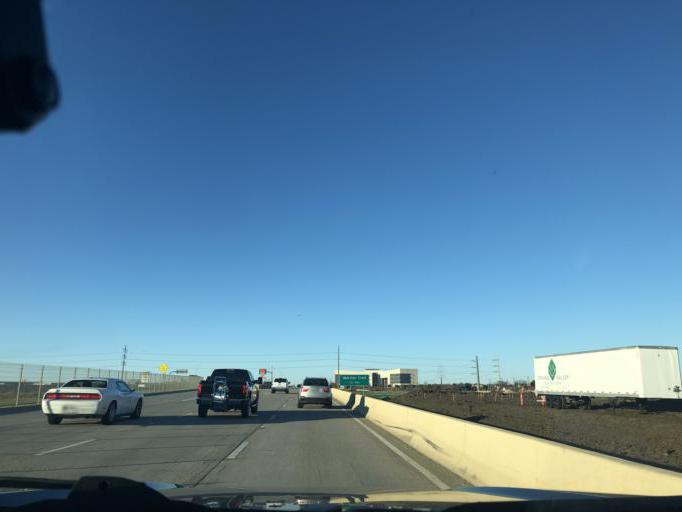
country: US
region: Texas
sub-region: Dallas County
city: Grand Prairie
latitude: 32.6937
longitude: -97.0239
